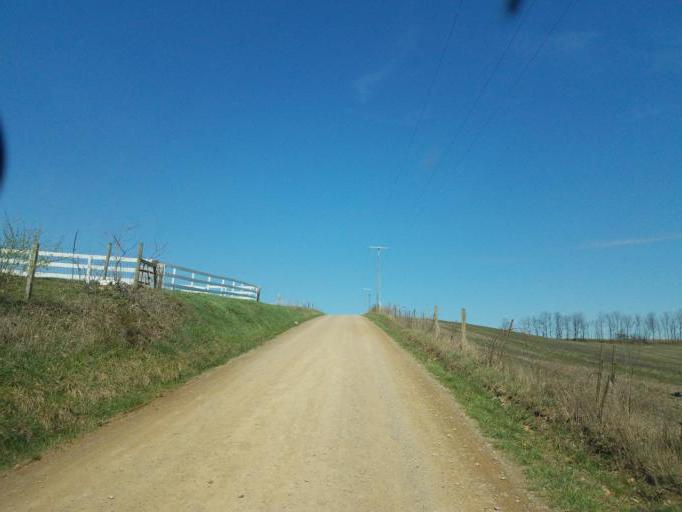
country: US
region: Ohio
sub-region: Knox County
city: Oak Hill
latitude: 40.3329
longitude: -82.1909
